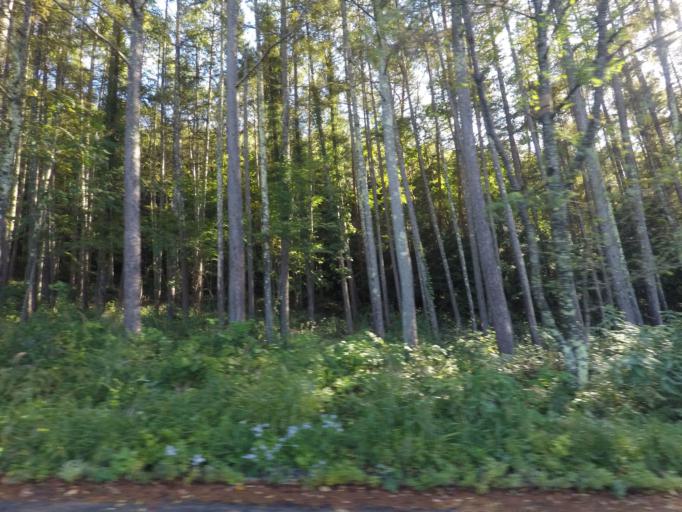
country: JP
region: Nagano
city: Ina
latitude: 35.9536
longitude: 137.7797
